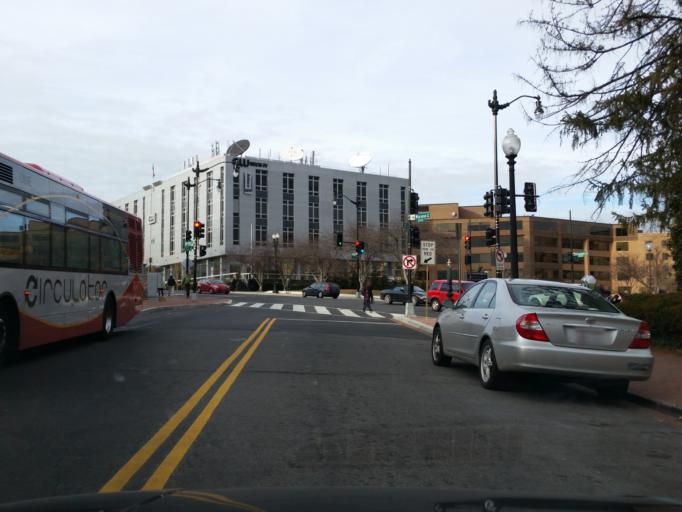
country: US
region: Washington, D.C.
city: Washington, D.C.
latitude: 38.9173
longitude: -77.0694
